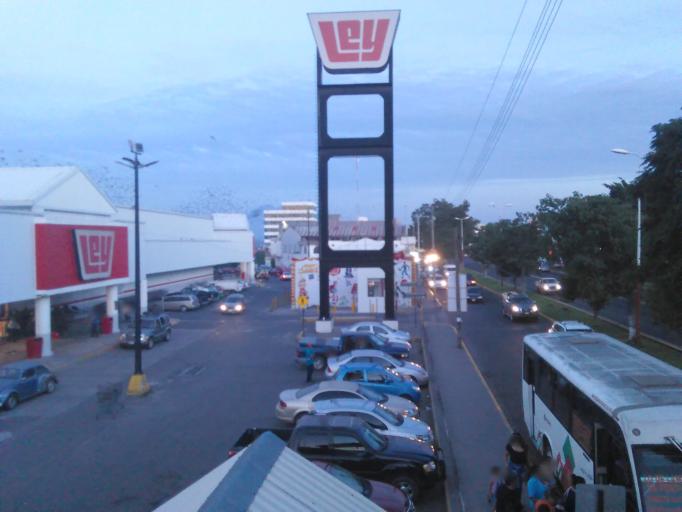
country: MX
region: Nayarit
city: Tepic
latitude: 21.5184
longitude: -104.9156
